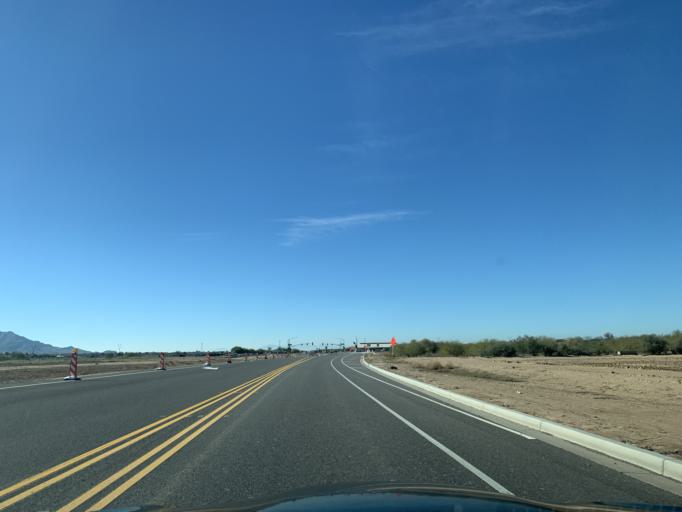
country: US
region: Arizona
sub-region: Maricopa County
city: Queen Creek
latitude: 33.2195
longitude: -111.6303
